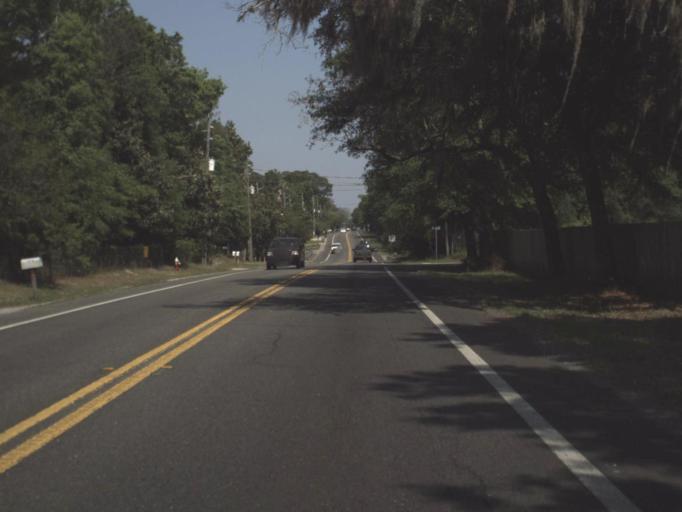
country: US
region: Florida
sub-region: Escambia County
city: Myrtle Grove
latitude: 30.3979
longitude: -87.4112
